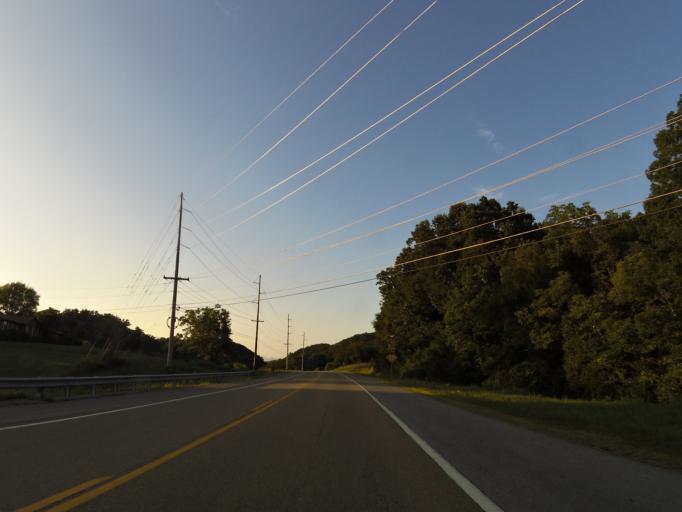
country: US
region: Tennessee
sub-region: Union County
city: Luttrell
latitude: 36.1809
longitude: -83.7408
